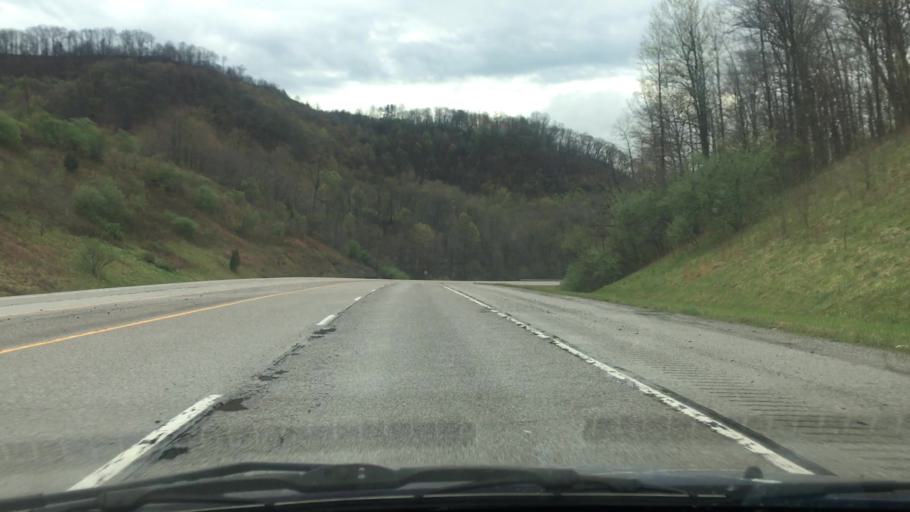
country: US
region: Kentucky
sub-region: Letcher County
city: Jenkins
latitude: 37.2133
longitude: -82.6249
